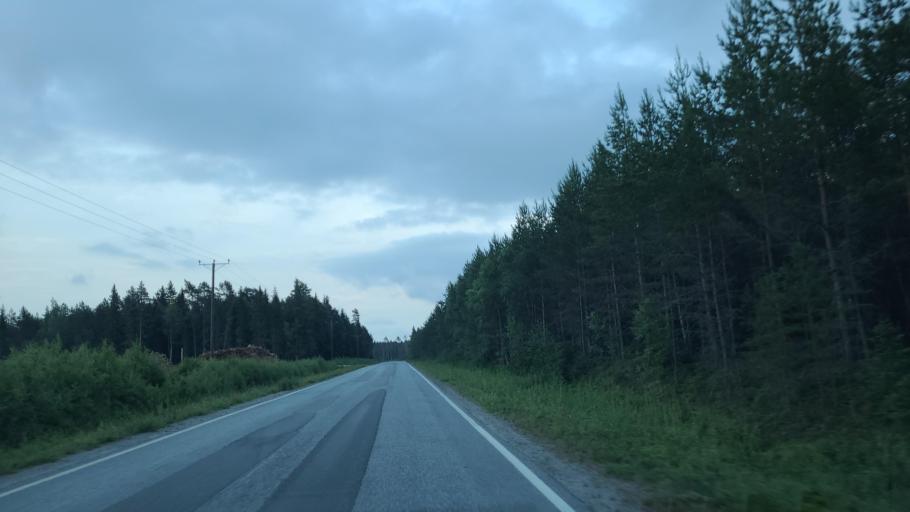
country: FI
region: Ostrobothnia
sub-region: Vaasa
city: Replot
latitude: 63.2068
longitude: 21.2628
